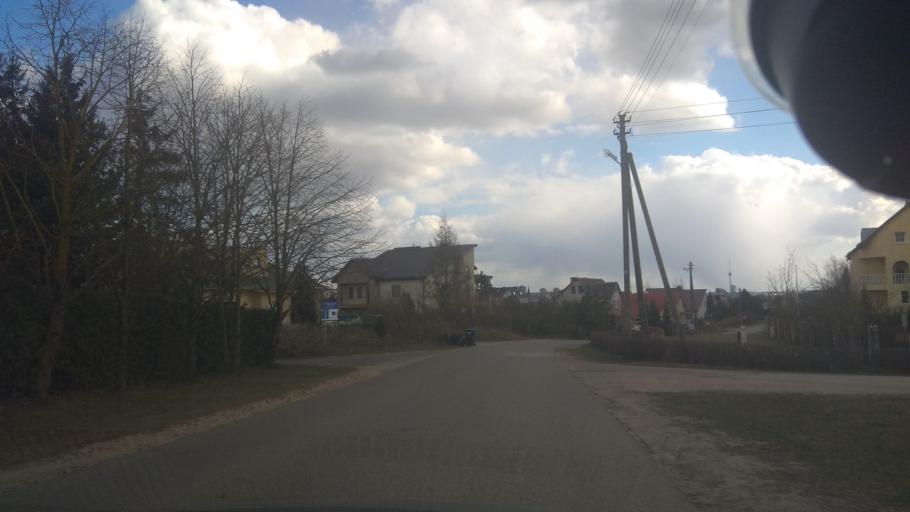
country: LT
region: Vilnius County
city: Pasilaiciai
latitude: 54.7406
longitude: 25.2019
